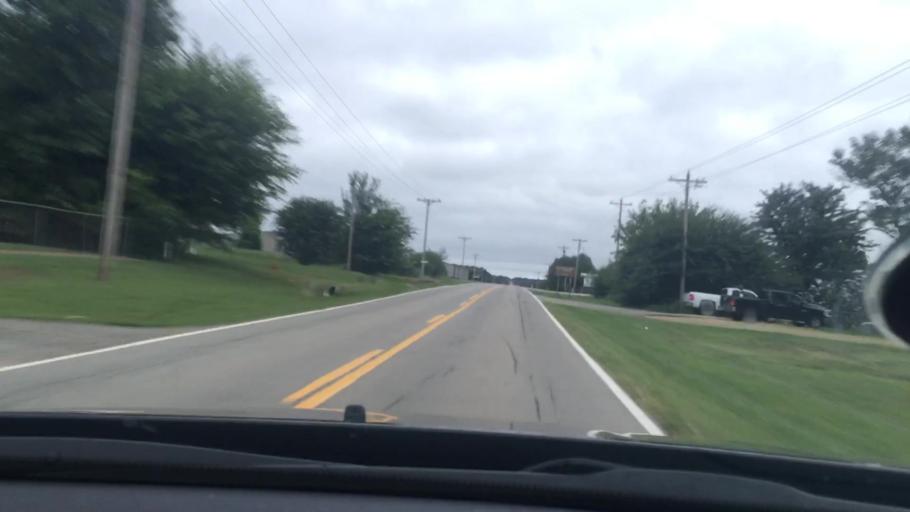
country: US
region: Oklahoma
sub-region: Sequoyah County
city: Vian
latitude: 35.6097
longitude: -94.9916
